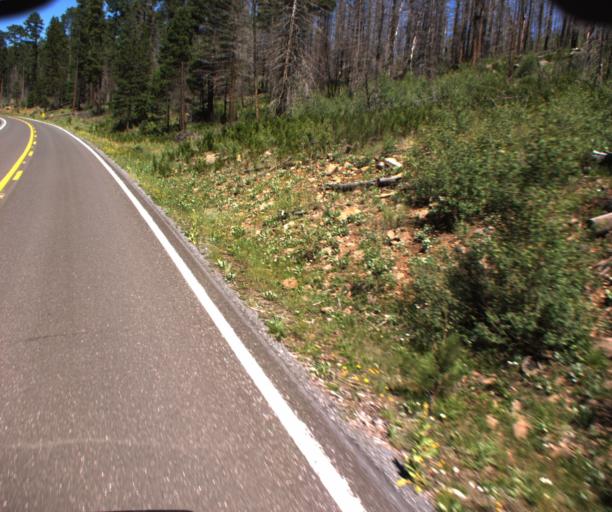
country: US
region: Arizona
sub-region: Apache County
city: Eagar
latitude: 33.6483
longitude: -109.2989
